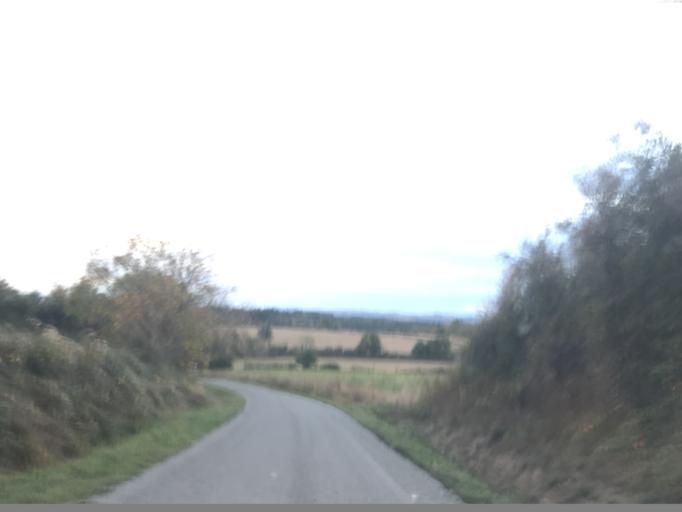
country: FR
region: Auvergne
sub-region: Departement du Puy-de-Dome
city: Escoutoux
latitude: 45.7766
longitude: 3.5960
